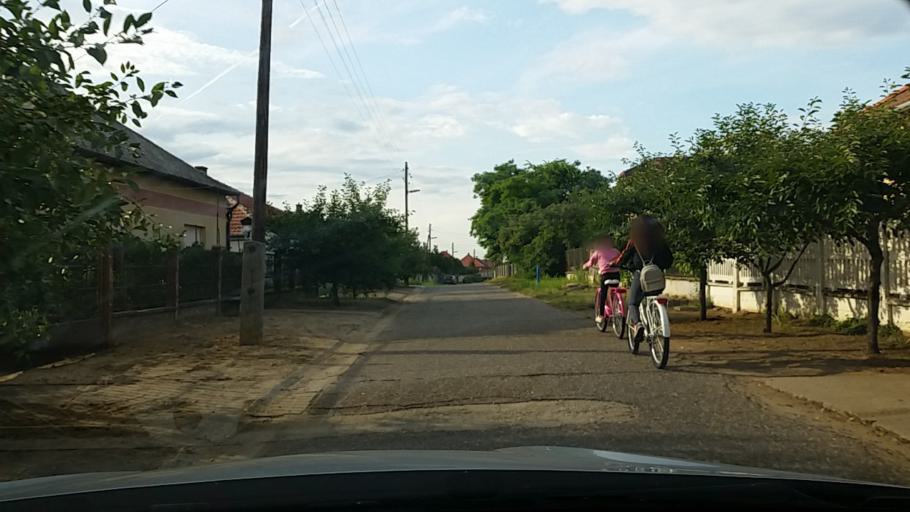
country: HU
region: Szabolcs-Szatmar-Bereg
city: Kek
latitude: 48.1166
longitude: 21.8822
